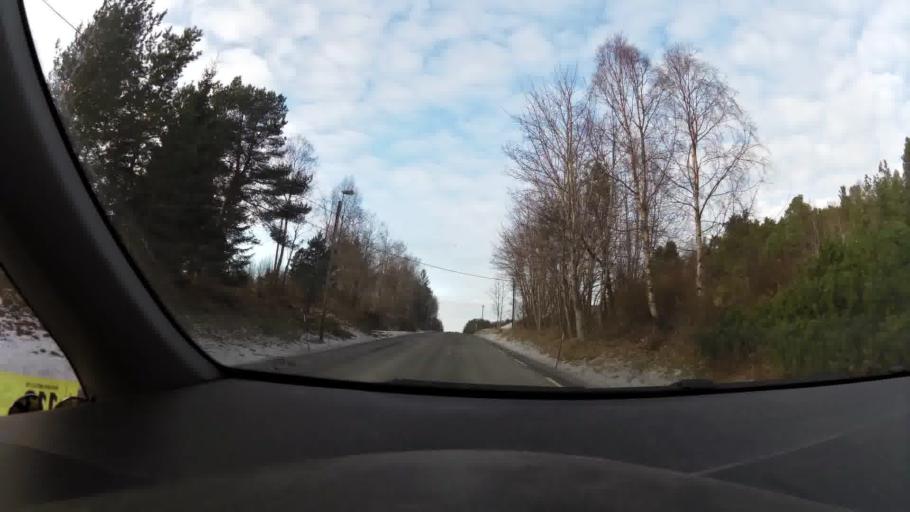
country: NO
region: More og Romsdal
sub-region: Kristiansund
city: Rensvik
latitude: 63.0895
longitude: 7.8526
